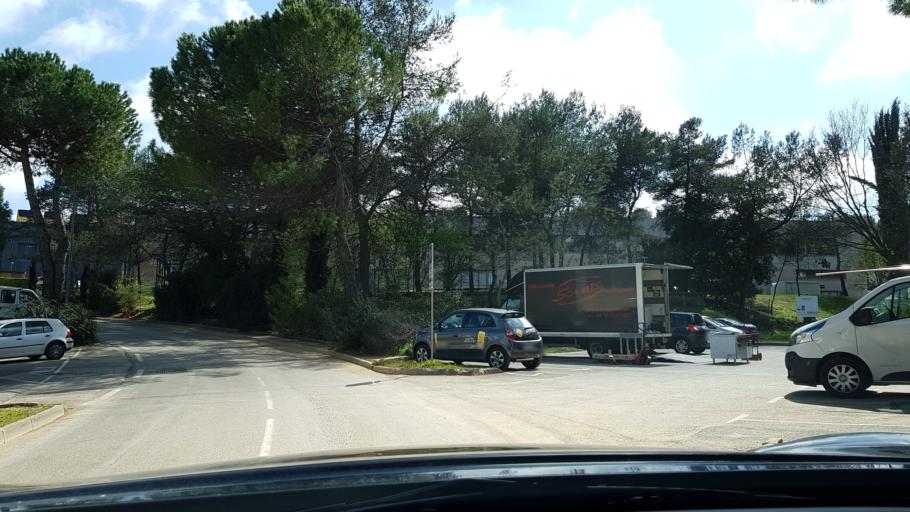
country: FR
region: Provence-Alpes-Cote d'Azur
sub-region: Departement des Alpes-Maritimes
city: Biot
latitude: 43.6090
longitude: 7.0736
